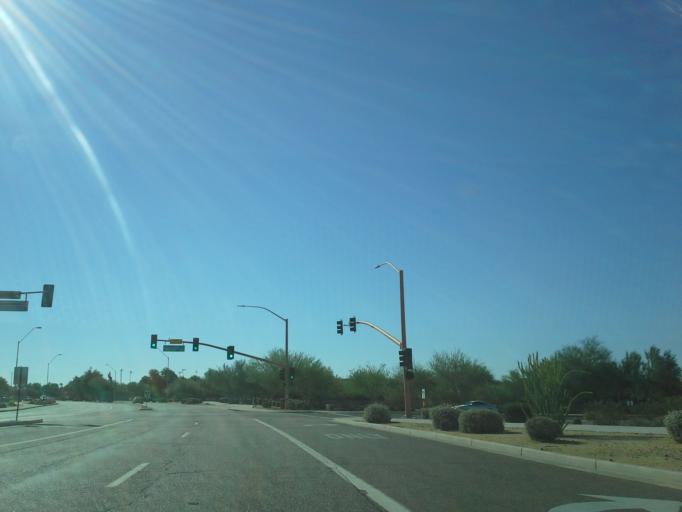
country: US
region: Arizona
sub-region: Maricopa County
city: Scottsdale
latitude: 33.6142
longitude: -111.8689
